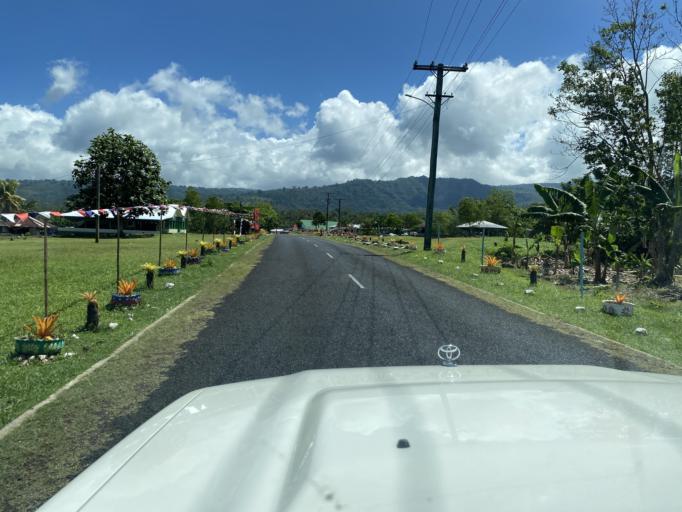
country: WS
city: Lotofaga
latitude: -13.9905
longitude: -171.8308
